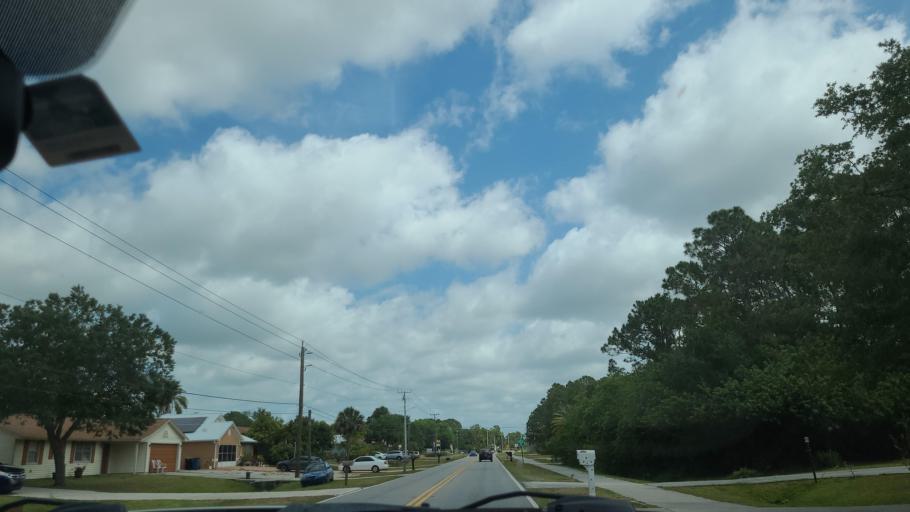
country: US
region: Florida
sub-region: Brevard County
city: June Park
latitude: 28.0194
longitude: -80.6967
